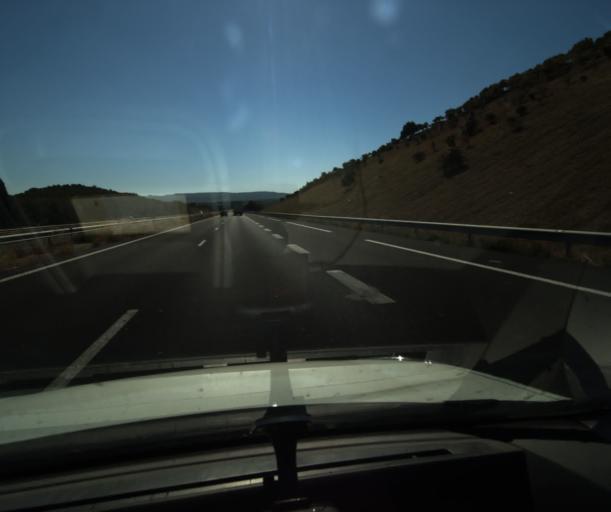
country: FR
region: Languedoc-Roussillon
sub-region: Departement de l'Aude
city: Narbonne
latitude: 43.1533
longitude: 2.9643
